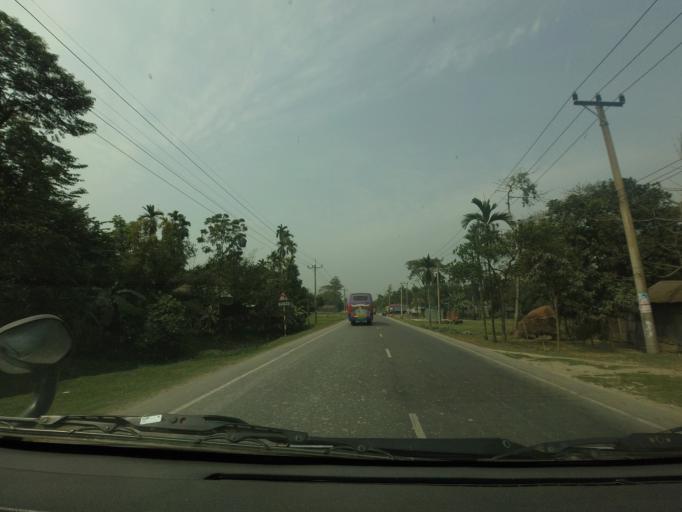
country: BD
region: Dhaka
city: Kishorganj
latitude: 24.3263
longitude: 90.7630
